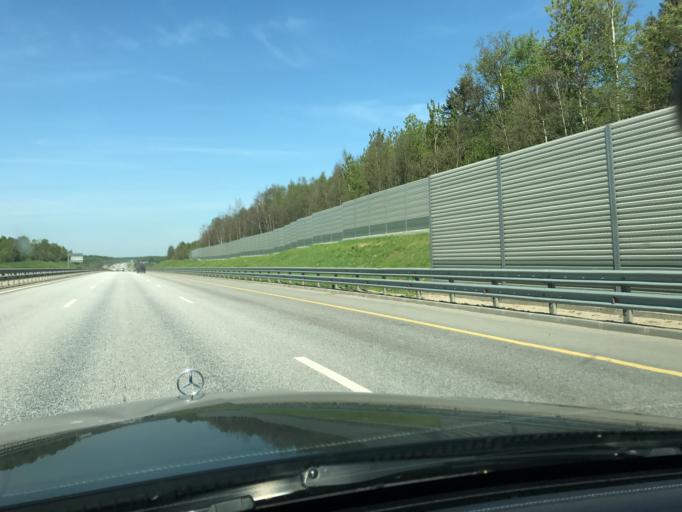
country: RU
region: Moskovskaya
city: Rumyantsevo
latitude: 55.9193
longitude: 36.5904
